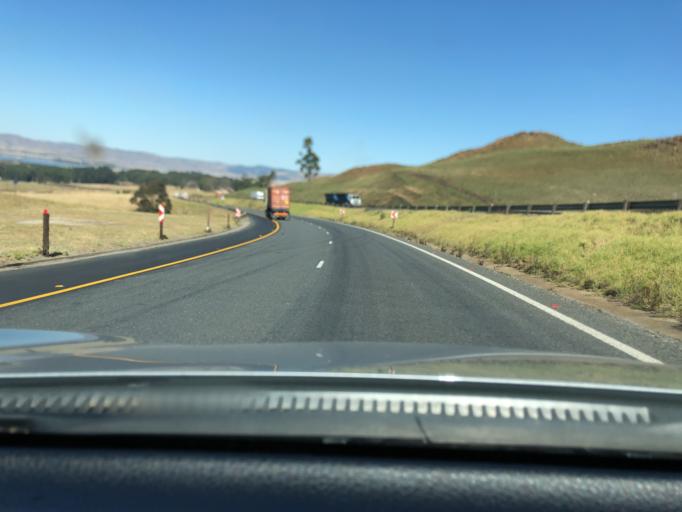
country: ZA
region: KwaZulu-Natal
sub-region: uMgungundlovu District Municipality
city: Howick
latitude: -29.4574
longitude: 30.1776
